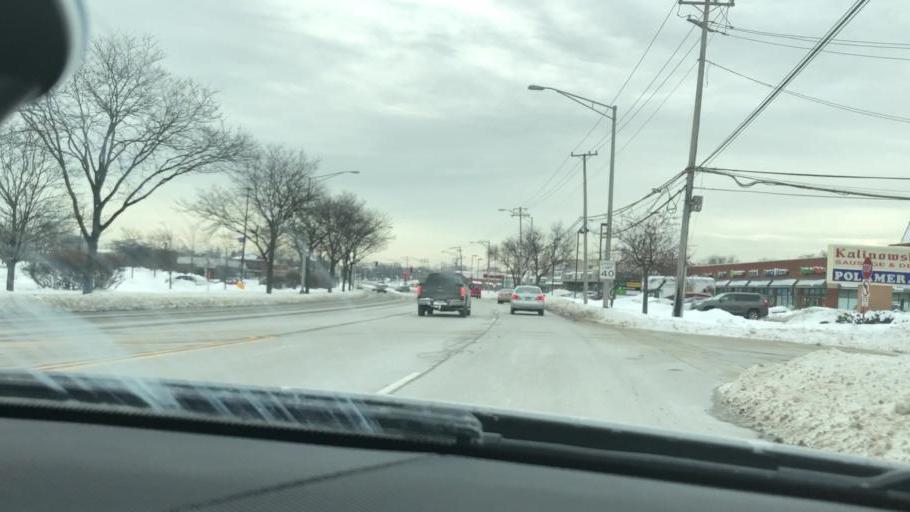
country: US
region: Illinois
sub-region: Cook County
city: Mount Prospect
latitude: 42.0681
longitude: -87.9245
